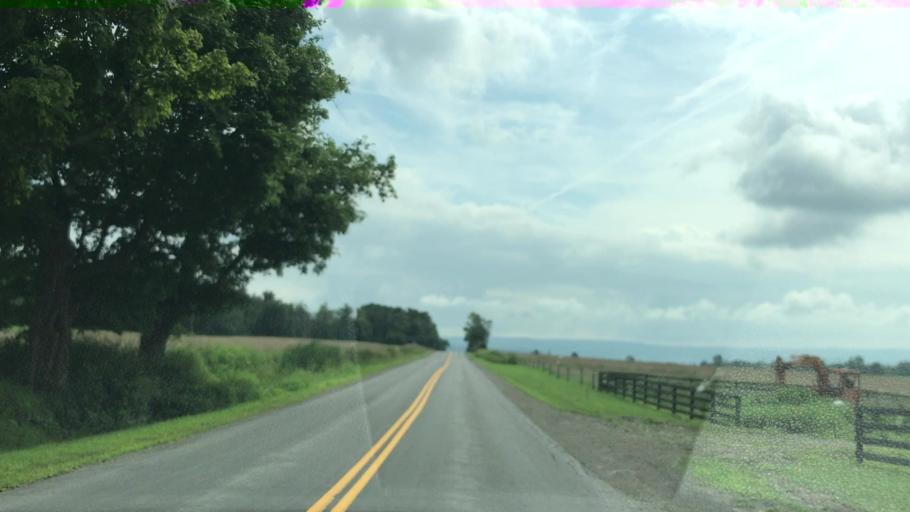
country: US
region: New York
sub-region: Steuben County
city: Sylvan Beach
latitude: 42.5118
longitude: -77.2153
